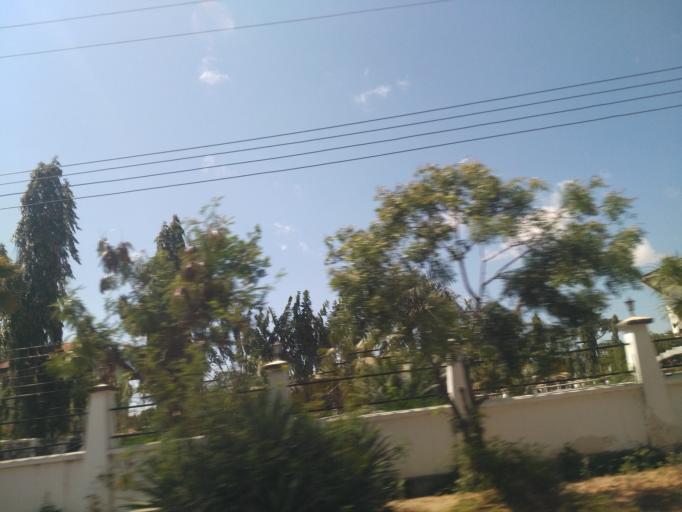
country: TZ
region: Dodoma
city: Dodoma
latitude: -6.1647
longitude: 35.7603
